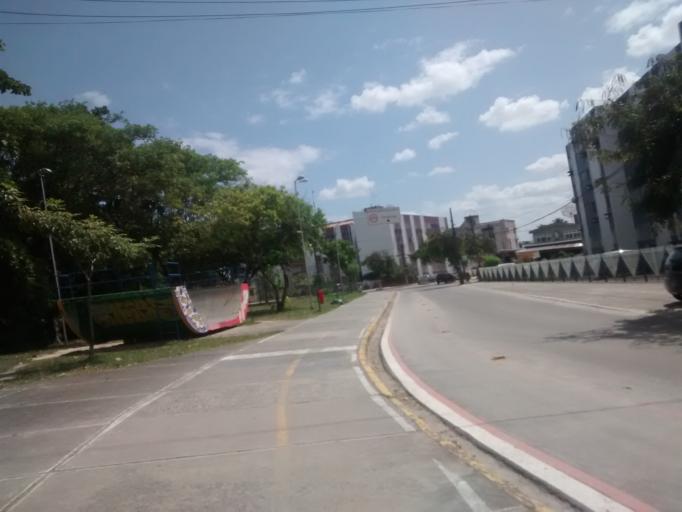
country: BR
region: Pernambuco
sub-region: Recife
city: Recife
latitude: -8.0925
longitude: -34.9153
